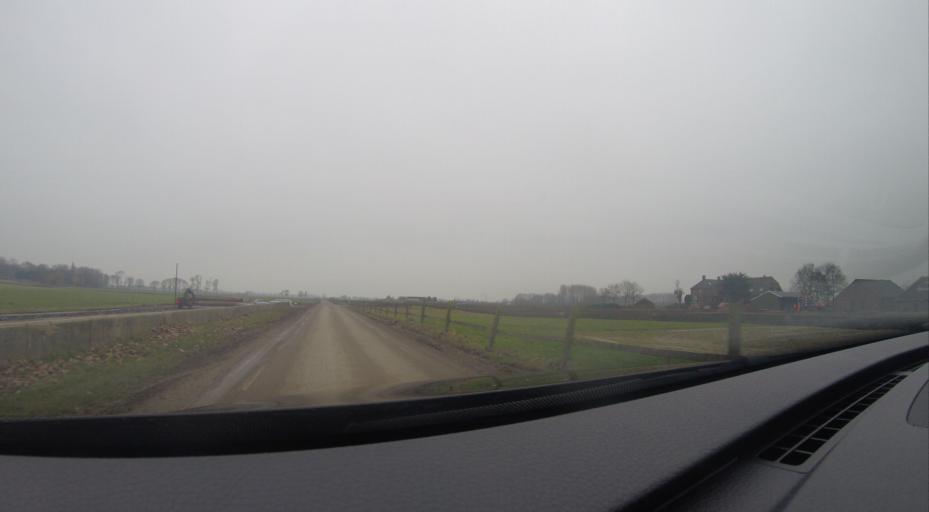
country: NL
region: Gelderland
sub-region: Gemeente Zutphen
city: Zutphen
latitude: 52.1141
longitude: 6.1837
